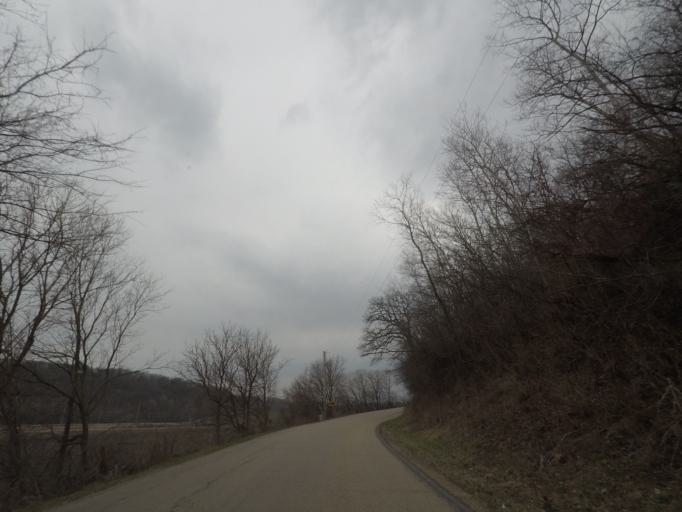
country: US
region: Wisconsin
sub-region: Dane County
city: Cross Plains
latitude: 43.0968
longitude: -89.6033
